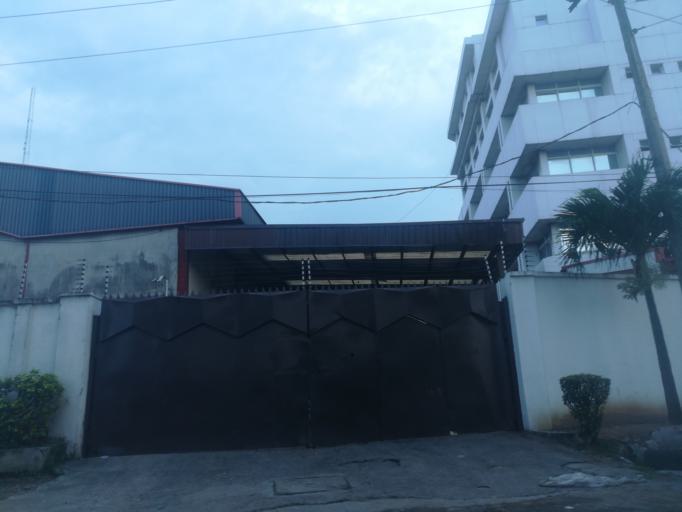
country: NG
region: Lagos
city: Somolu
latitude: 6.5519
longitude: 3.3786
